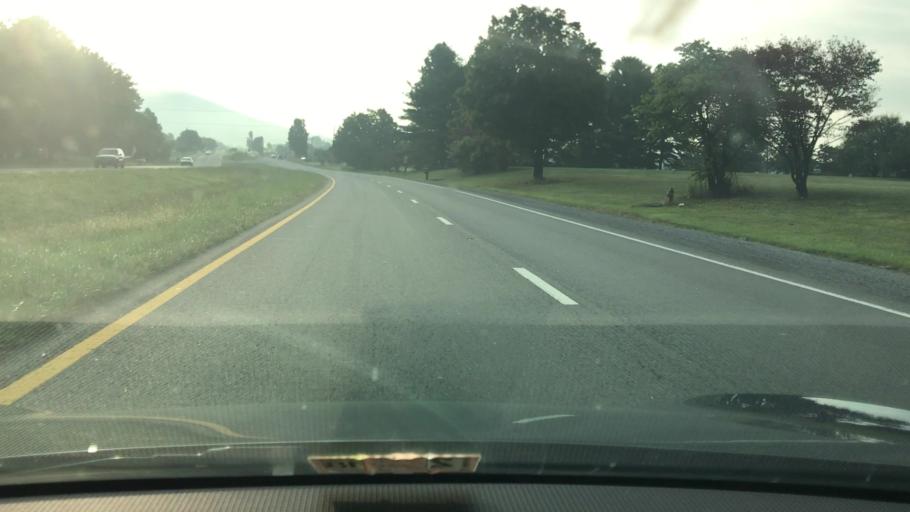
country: US
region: Virginia
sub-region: Botetourt County
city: Blue Ridge
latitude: 37.3797
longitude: -79.7200
